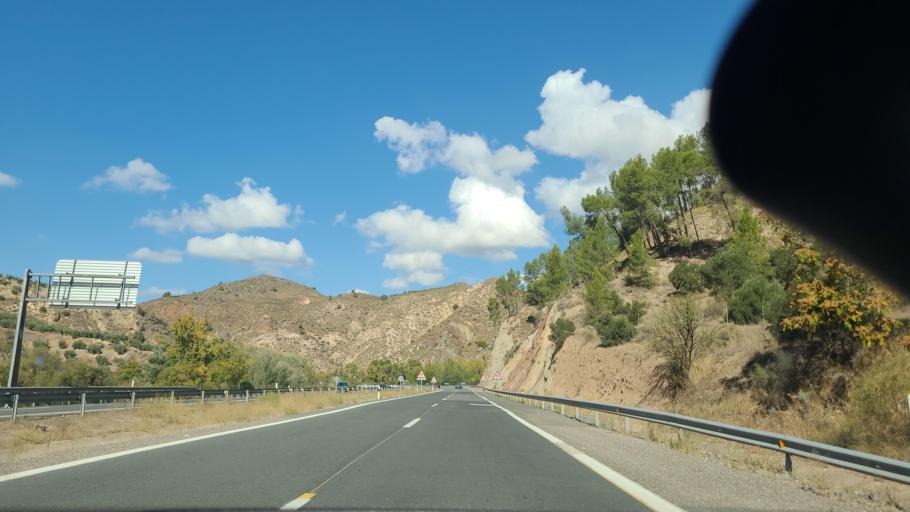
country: ES
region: Andalusia
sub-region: Provincia de Jaen
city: Cambil
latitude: 37.6516
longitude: -3.6056
